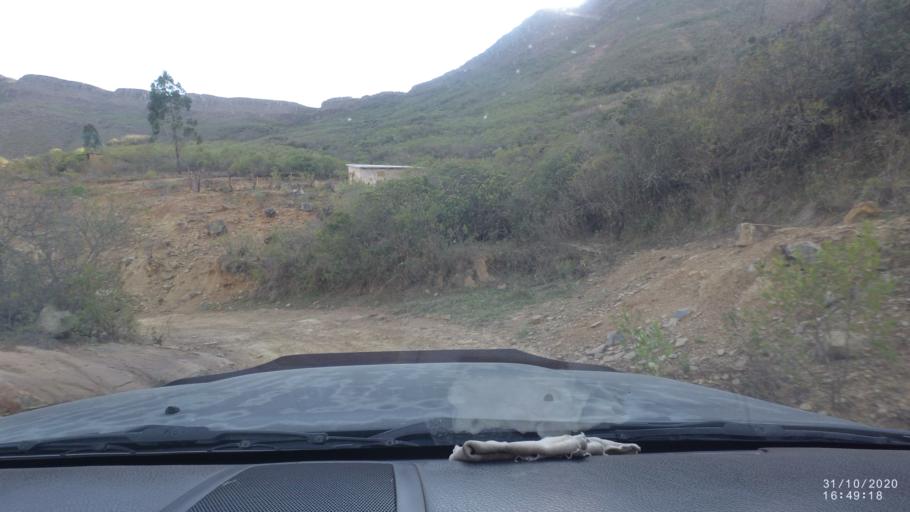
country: BO
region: Chuquisaca
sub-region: Provincia Zudanez
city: Mojocoya
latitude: -18.5065
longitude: -64.5721
